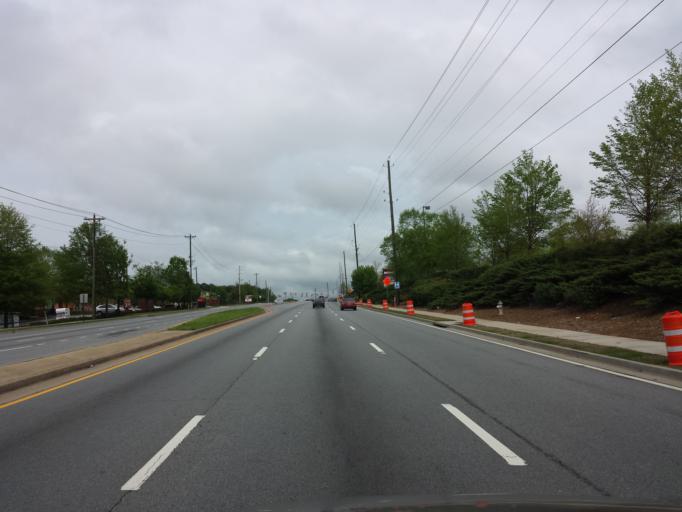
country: US
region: Georgia
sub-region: Cobb County
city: Mableton
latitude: 33.8540
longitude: -84.6077
